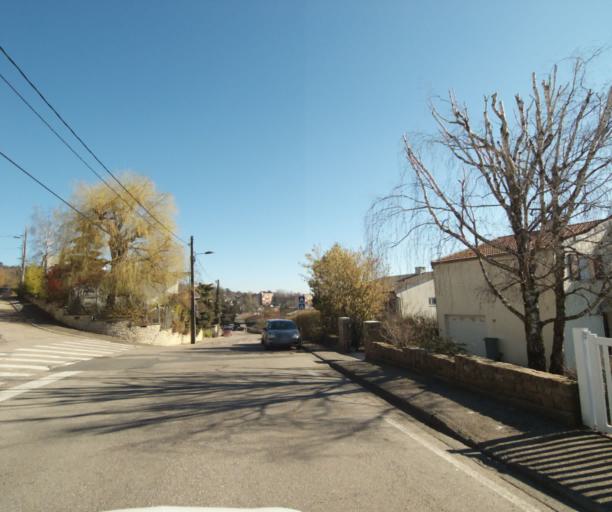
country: FR
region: Lorraine
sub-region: Departement de Meurthe-et-Moselle
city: Saint-Max
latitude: 48.7106
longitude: 6.1999
